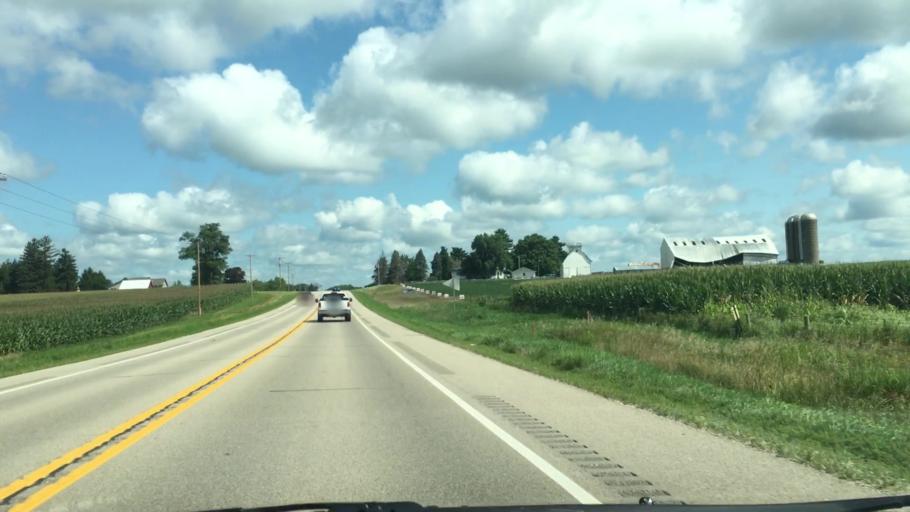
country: US
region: Iowa
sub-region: Johnson County
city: Solon
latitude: 41.8195
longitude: -91.4964
